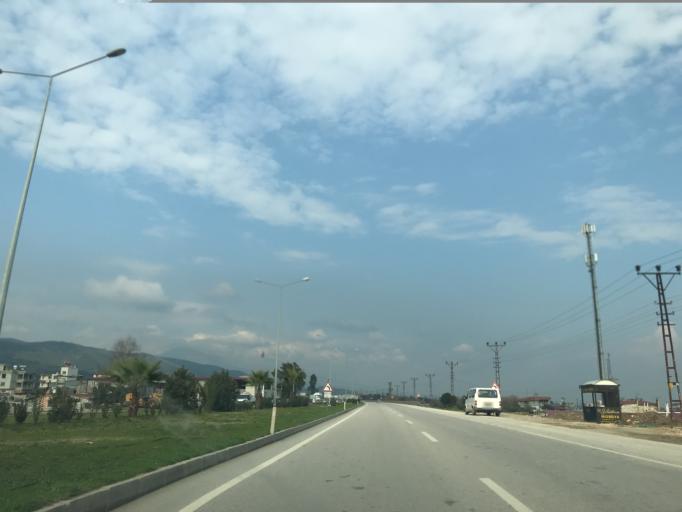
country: TR
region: Hatay
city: Serinyol
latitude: 36.3586
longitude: 36.2197
